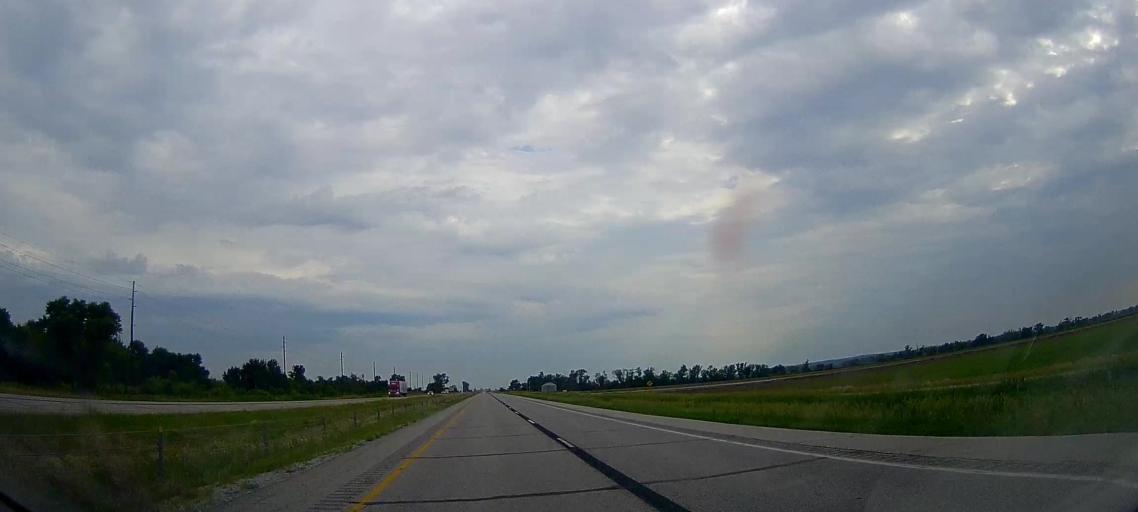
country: US
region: Iowa
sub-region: Harrison County
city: Missouri Valley
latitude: 41.4730
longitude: -95.8997
